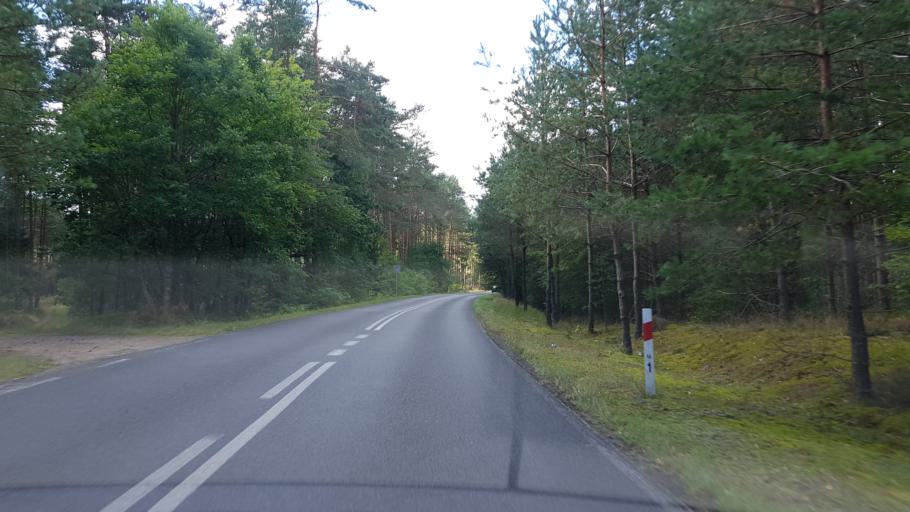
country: PL
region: West Pomeranian Voivodeship
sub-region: Powiat koszalinski
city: Sianow
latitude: 54.0889
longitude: 16.3453
